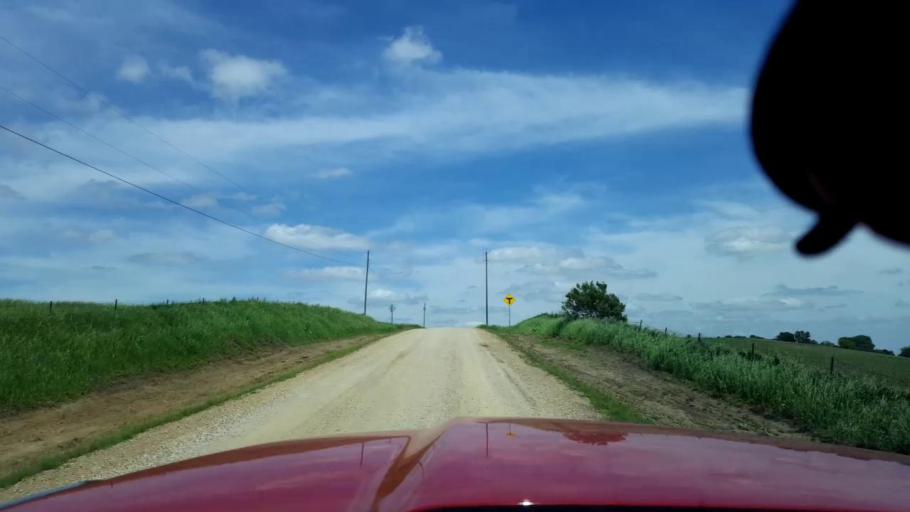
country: US
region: Iowa
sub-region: Linn County
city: Lisbon
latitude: 41.9510
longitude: -91.3501
